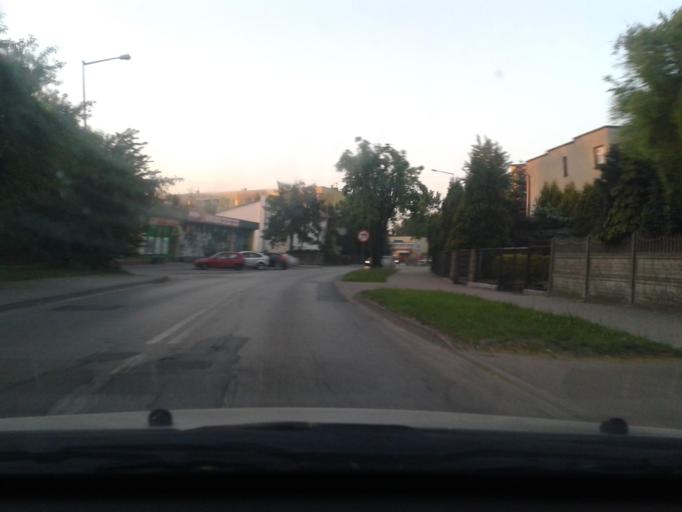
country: PL
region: Lesser Poland Voivodeship
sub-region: Powiat oswiecimski
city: Oswiecim
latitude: 50.0453
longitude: 19.2128
